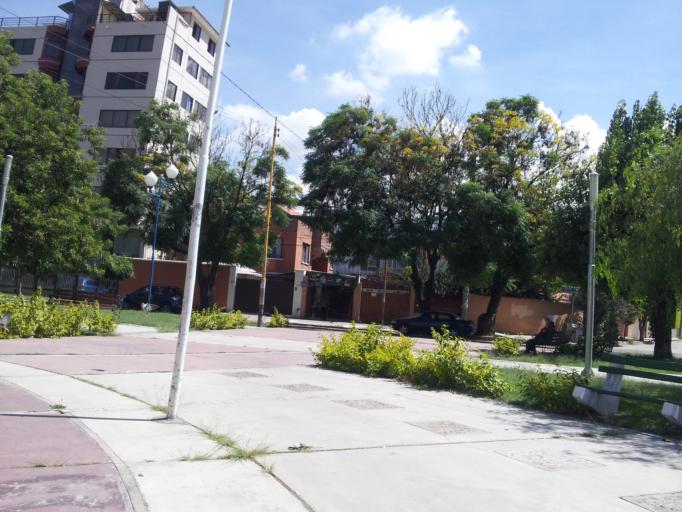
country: BO
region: Cochabamba
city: Cochabamba
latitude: -17.3854
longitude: -66.1732
